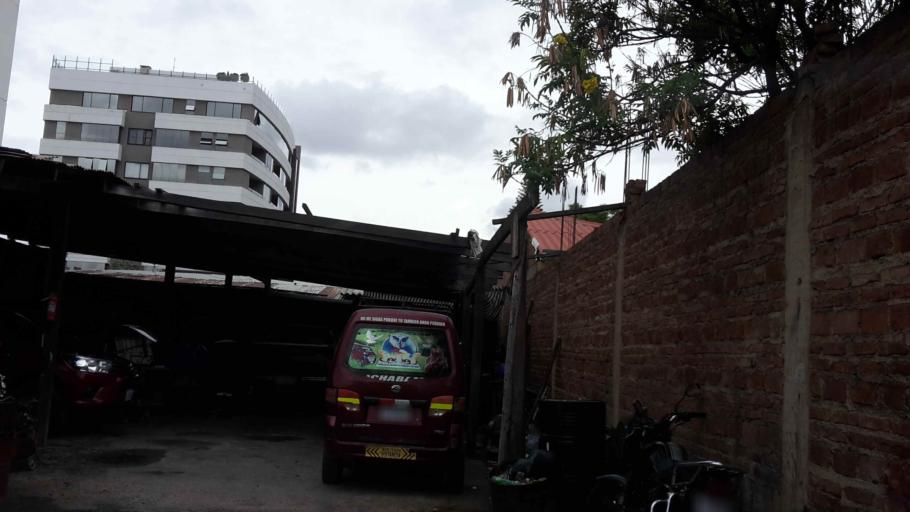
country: BO
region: Cochabamba
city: Cochabamba
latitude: -17.3706
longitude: -66.1447
